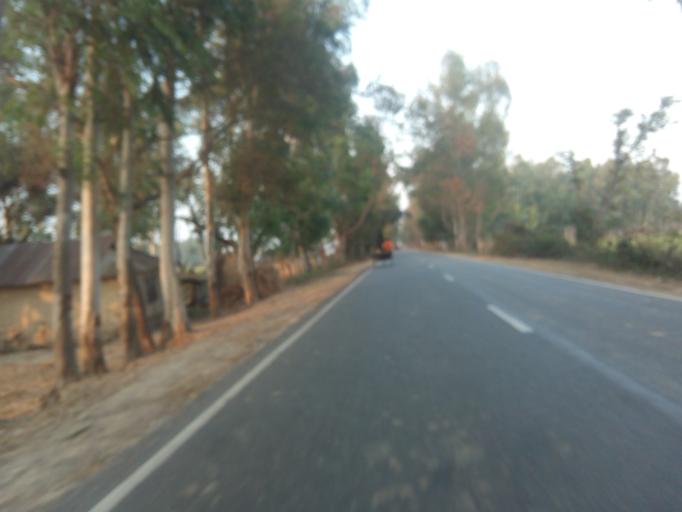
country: BD
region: Rajshahi
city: Bogra
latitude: 24.6304
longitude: 89.2456
